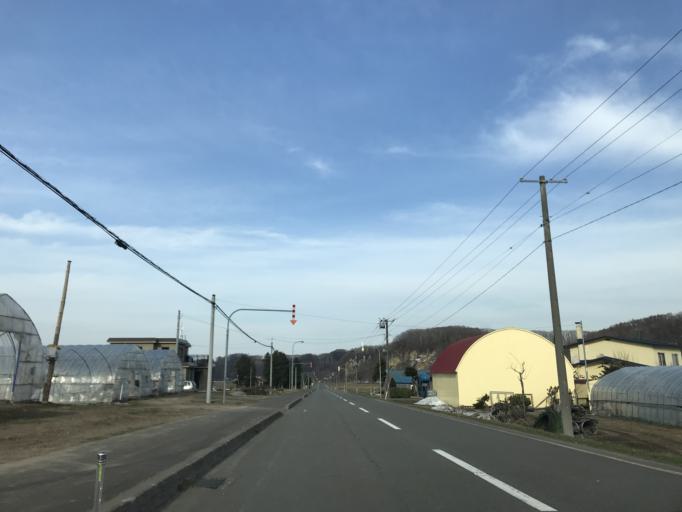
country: JP
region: Hokkaido
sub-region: Asahikawa-shi
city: Asahikawa
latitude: 43.6984
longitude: 142.3391
